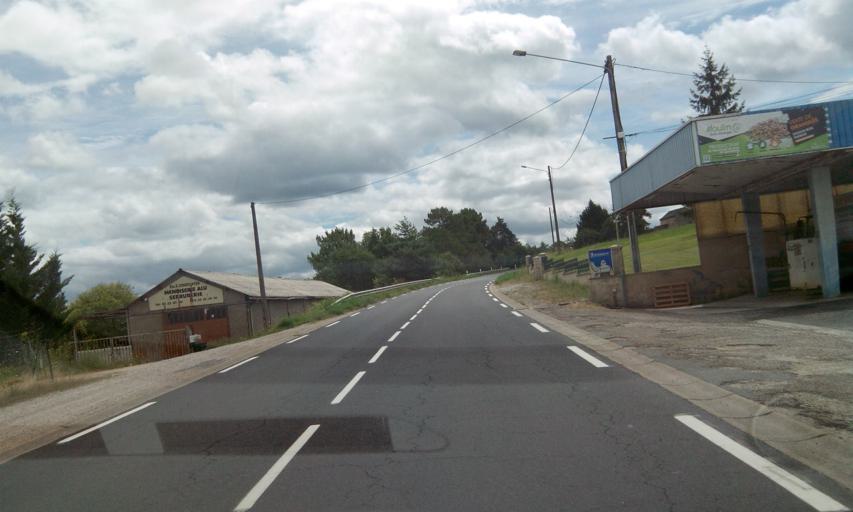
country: FR
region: Limousin
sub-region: Departement de la Correze
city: Cosnac
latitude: 45.1161
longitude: 1.5603
